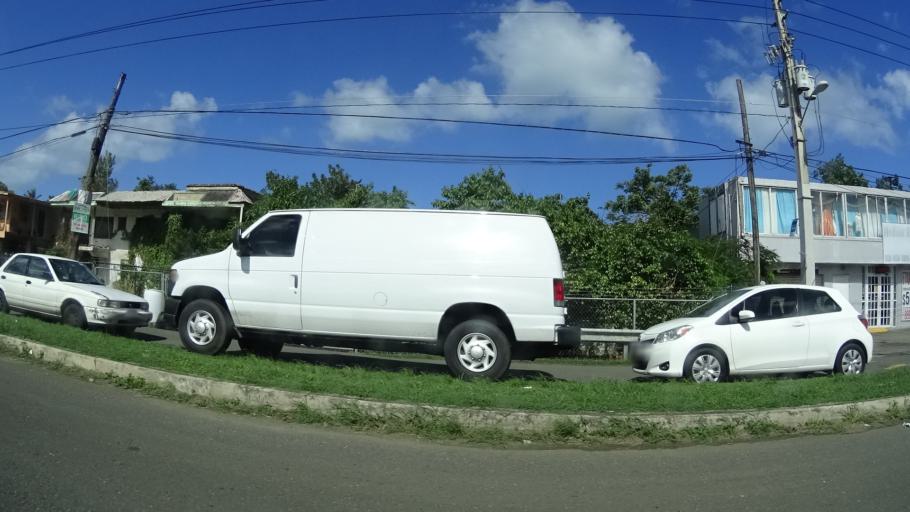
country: PR
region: Luquillo
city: Playa Fortuna
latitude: 18.3794
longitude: -65.7439
